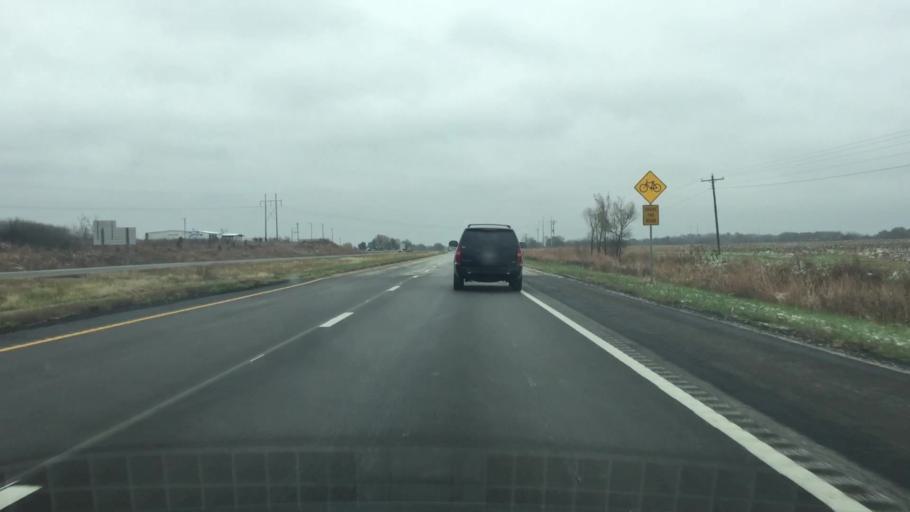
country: US
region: Missouri
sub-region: Saint Clair County
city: Osceola
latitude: 38.0349
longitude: -93.6785
